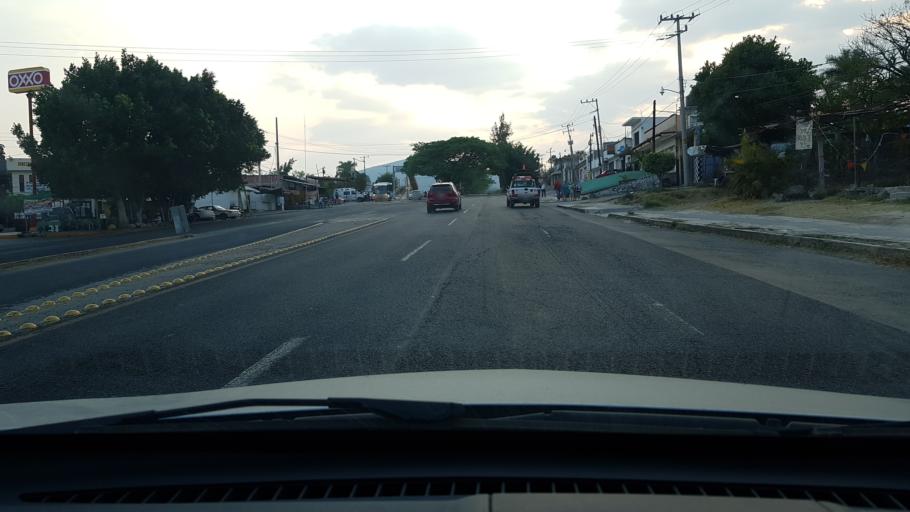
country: MX
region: Morelos
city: Yautepec
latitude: 18.8704
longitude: -99.0799
